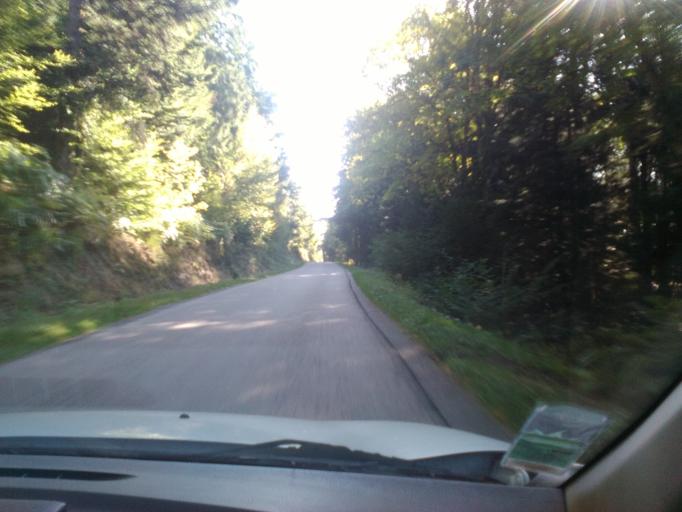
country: FR
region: Lorraine
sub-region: Departement des Vosges
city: Vagney
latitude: 48.0388
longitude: 6.7331
